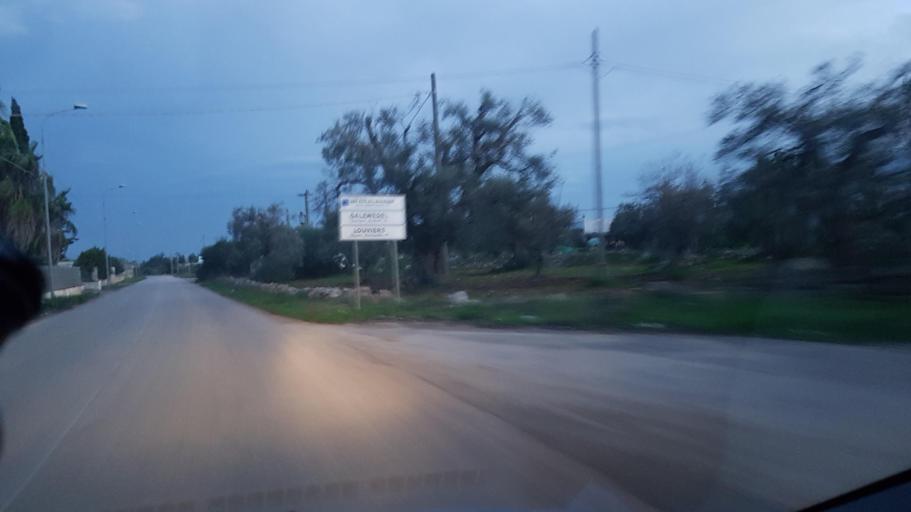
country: IT
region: Apulia
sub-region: Provincia di Brindisi
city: San Vito dei Normanni
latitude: 40.6496
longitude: 17.6939
